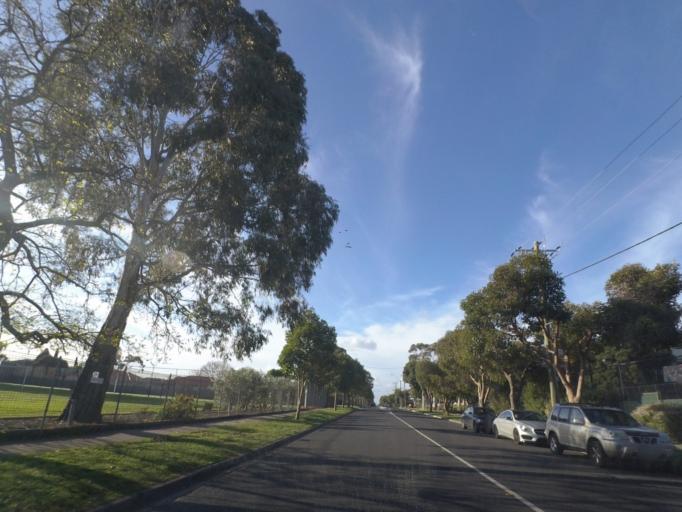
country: AU
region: Victoria
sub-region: Whitehorse
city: Box Hill
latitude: -37.8177
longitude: 145.1308
